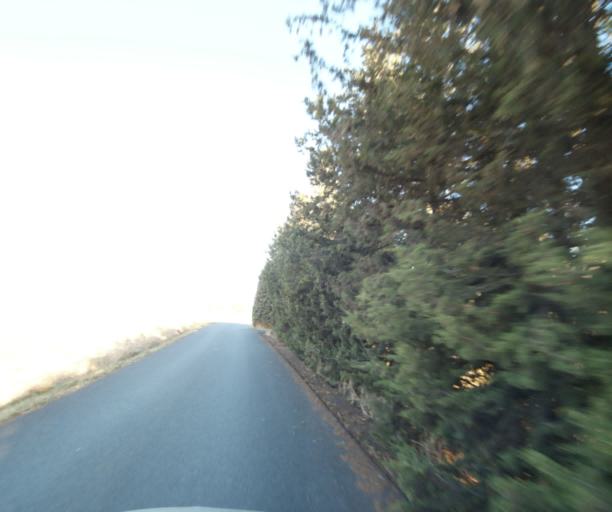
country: FR
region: Languedoc-Roussillon
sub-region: Departement du Gard
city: Bouillargues
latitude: 43.7894
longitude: 4.4445
